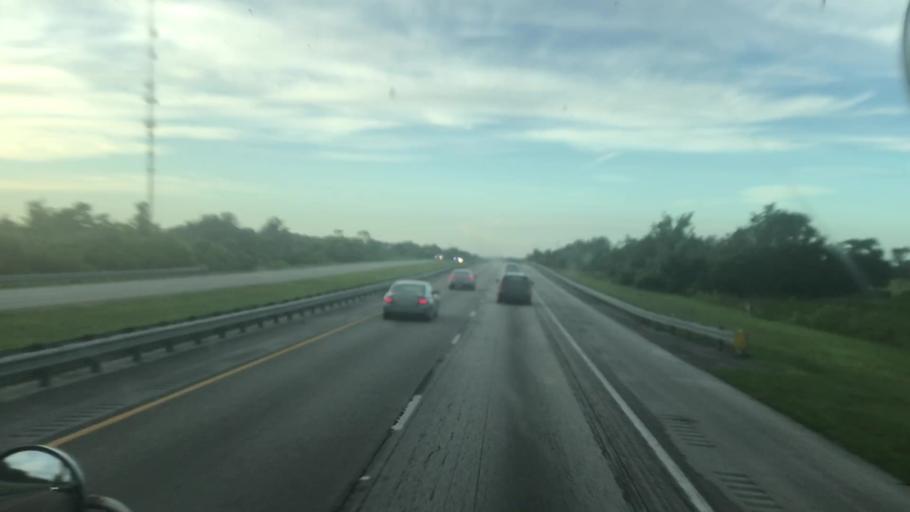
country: US
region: Florida
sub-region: Indian River County
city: Fellsmere
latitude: 27.7227
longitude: -80.9076
